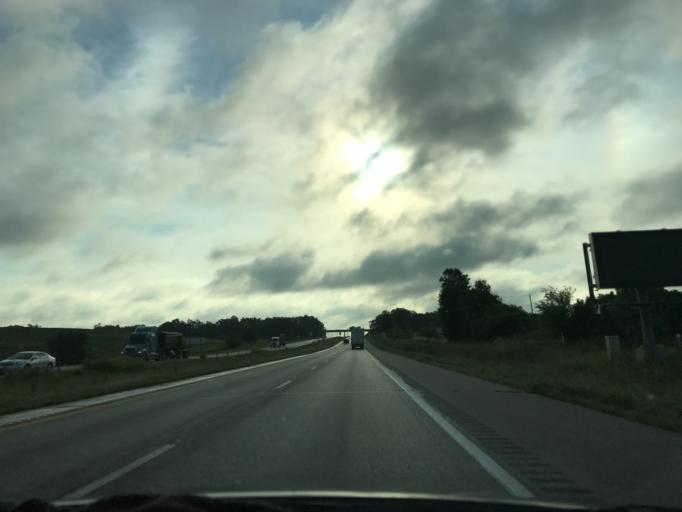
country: US
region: Iowa
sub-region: Johnson County
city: Tiffin
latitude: 41.6940
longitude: -91.6541
